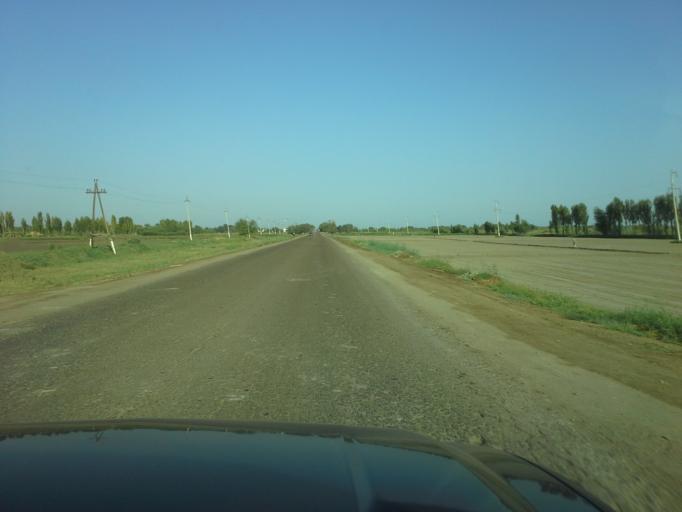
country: TM
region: Dasoguz
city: Boldumsaz
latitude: 42.2150
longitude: 59.5038
